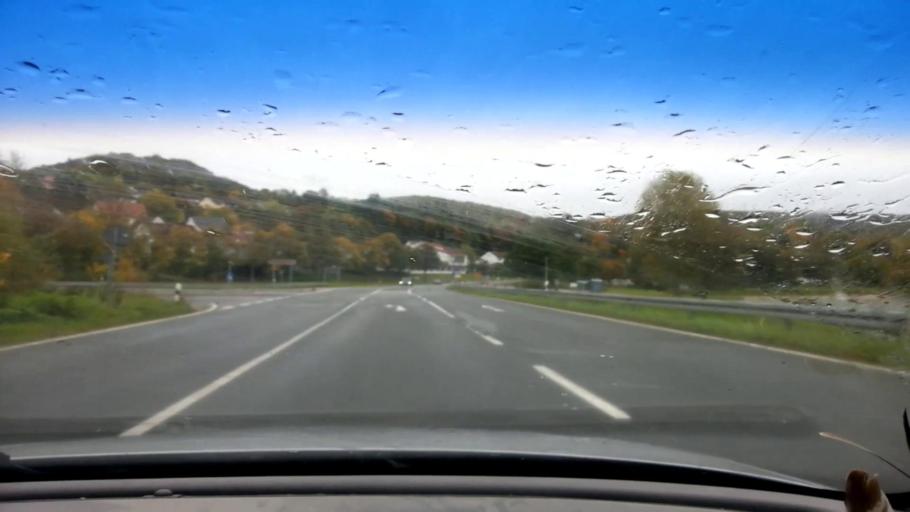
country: DE
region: Bavaria
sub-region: Upper Franconia
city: Heiligenstadt
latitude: 49.8674
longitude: 11.1648
